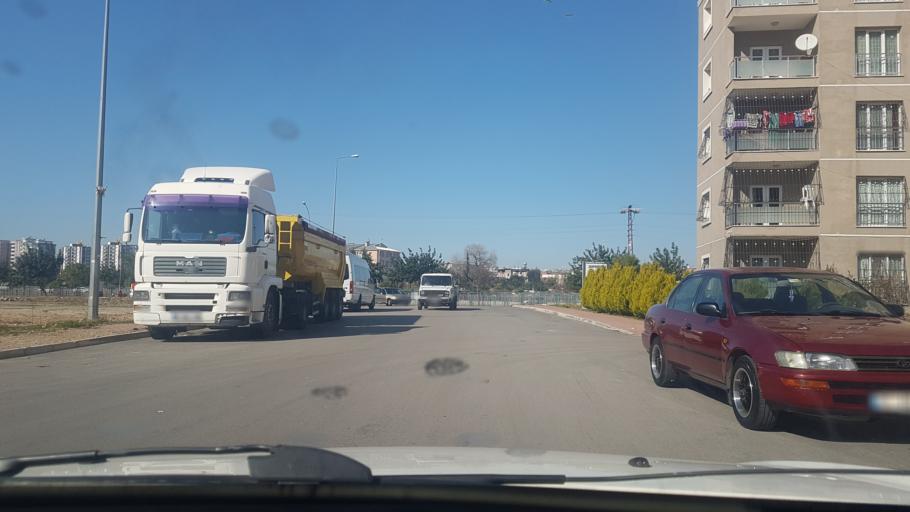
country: TR
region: Adana
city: Seyhan
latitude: 37.0105
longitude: 35.2761
